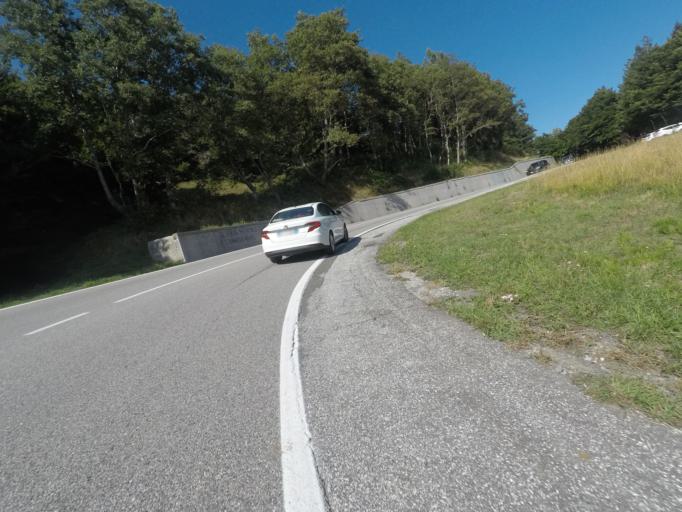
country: IT
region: Emilia-Romagna
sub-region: Provincia di Reggio Emilia
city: Collagna
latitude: 44.2997
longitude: 10.2115
